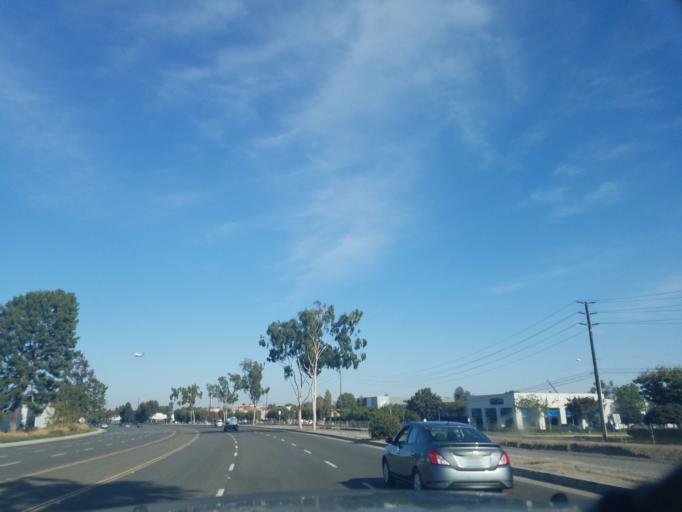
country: US
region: California
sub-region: Orange County
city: Irvine
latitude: 33.6892
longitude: -117.8534
